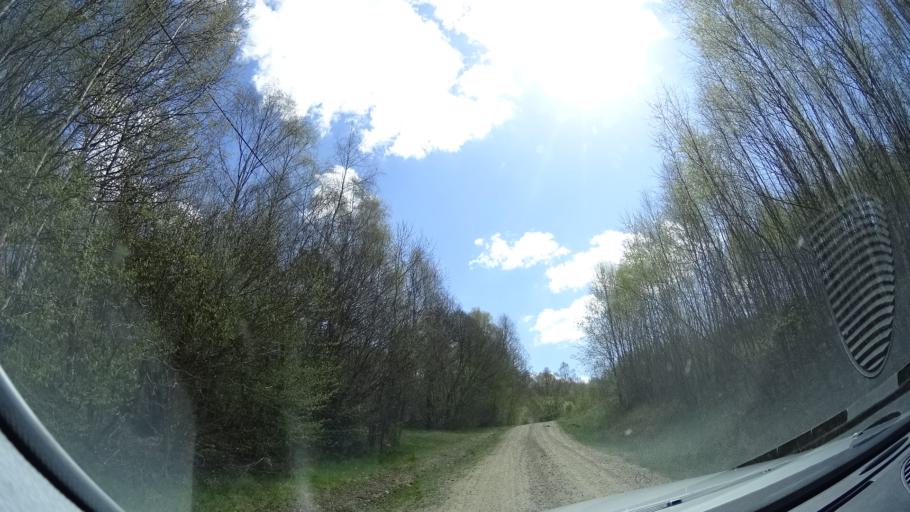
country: SE
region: Skane
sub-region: Hassleholms Kommun
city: Tormestorp
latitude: 56.0935
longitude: 13.7183
